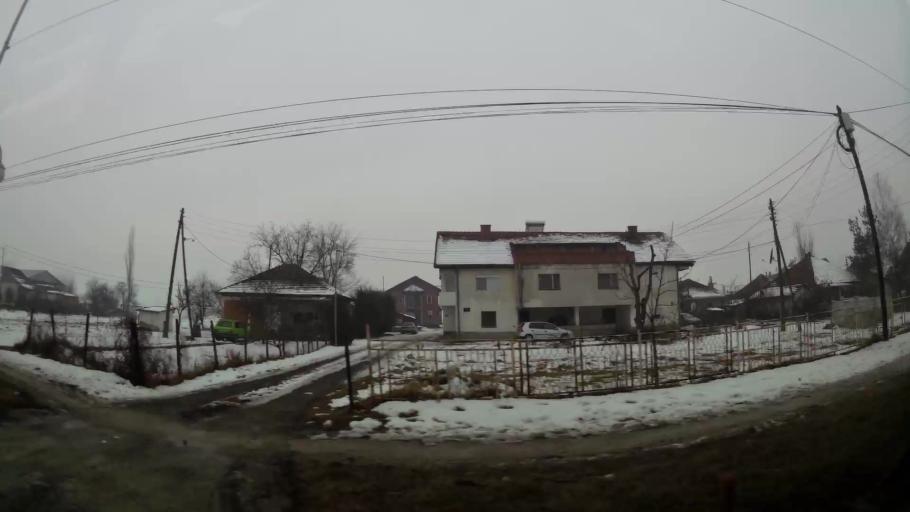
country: MK
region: Petrovec
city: Petrovec
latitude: 41.9316
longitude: 21.6242
